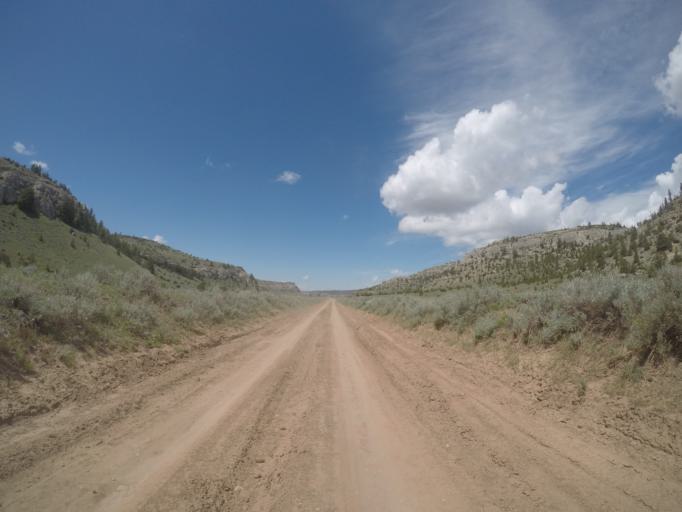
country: US
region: Wyoming
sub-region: Big Horn County
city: Lovell
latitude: 45.2308
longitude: -108.6078
